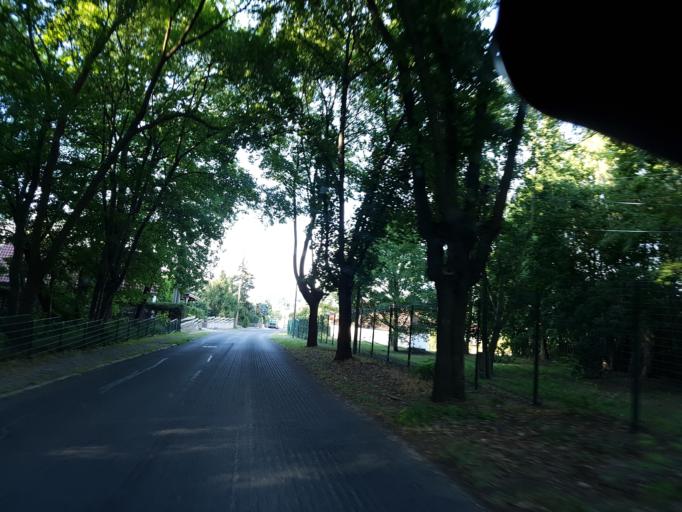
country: DE
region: Brandenburg
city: Elsterwerda
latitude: 51.4750
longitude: 13.5050
